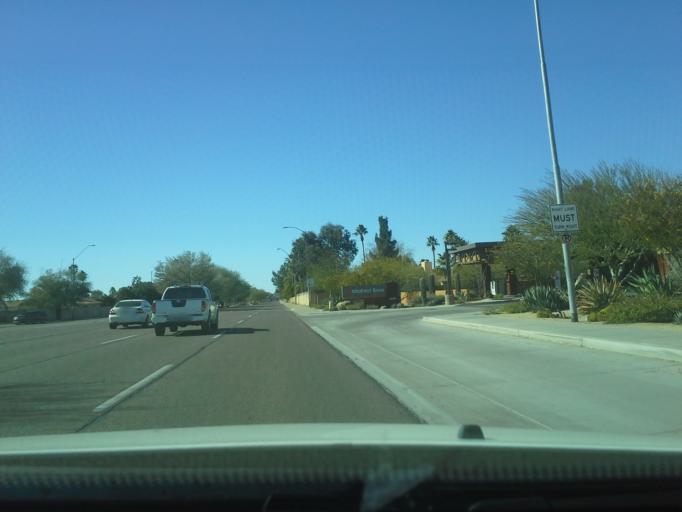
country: US
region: Arizona
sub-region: Maricopa County
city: Paradise Valley
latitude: 33.6261
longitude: -111.9441
